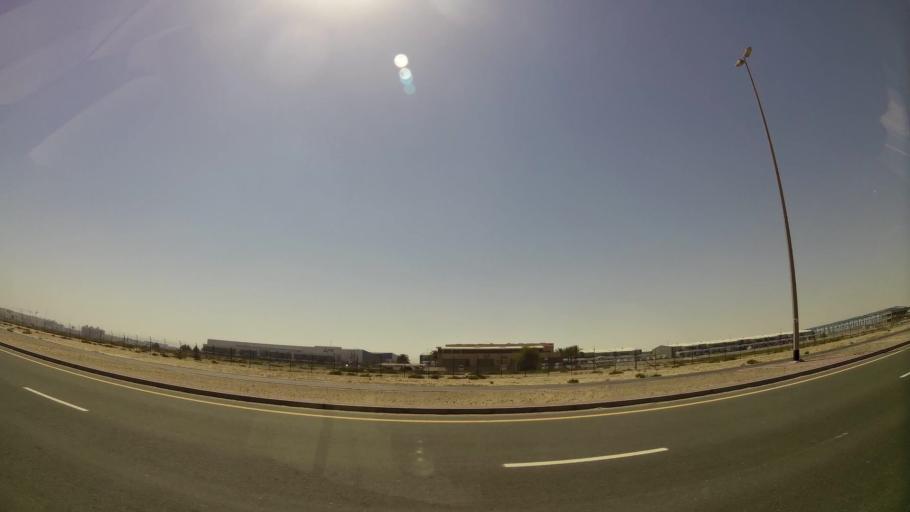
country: AE
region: Dubai
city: Dubai
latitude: 24.9733
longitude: 55.1289
